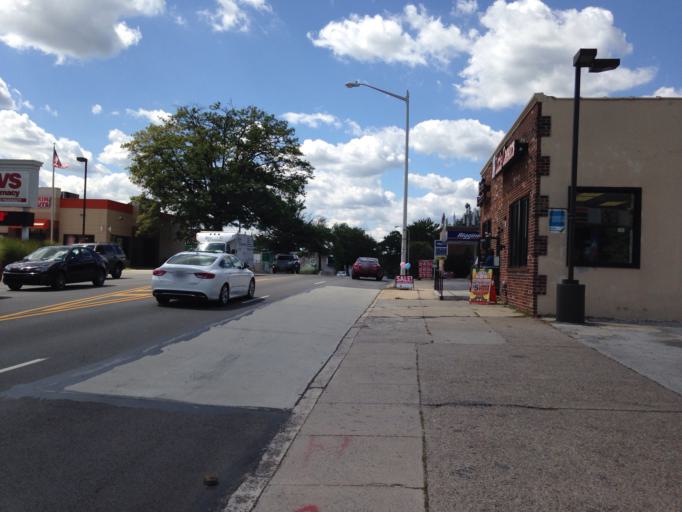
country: US
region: Pennsylvania
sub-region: Montgomery County
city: Penn Wynne
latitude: 39.9800
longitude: -75.2699
